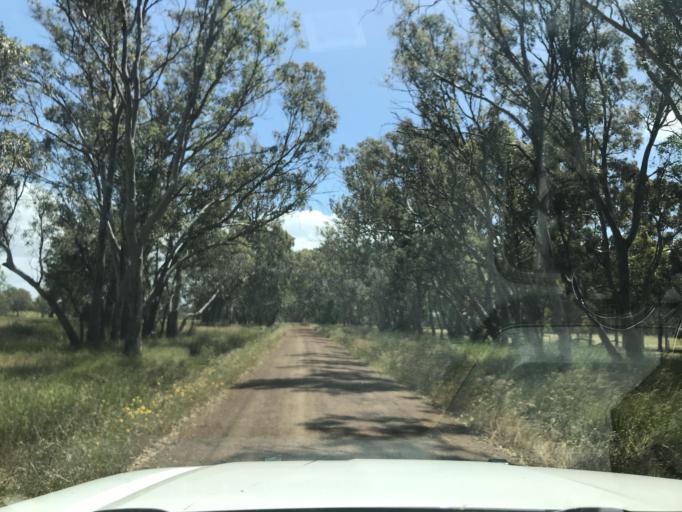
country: AU
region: South Australia
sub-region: Wattle Range
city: Penola
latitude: -37.2866
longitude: 141.4911
